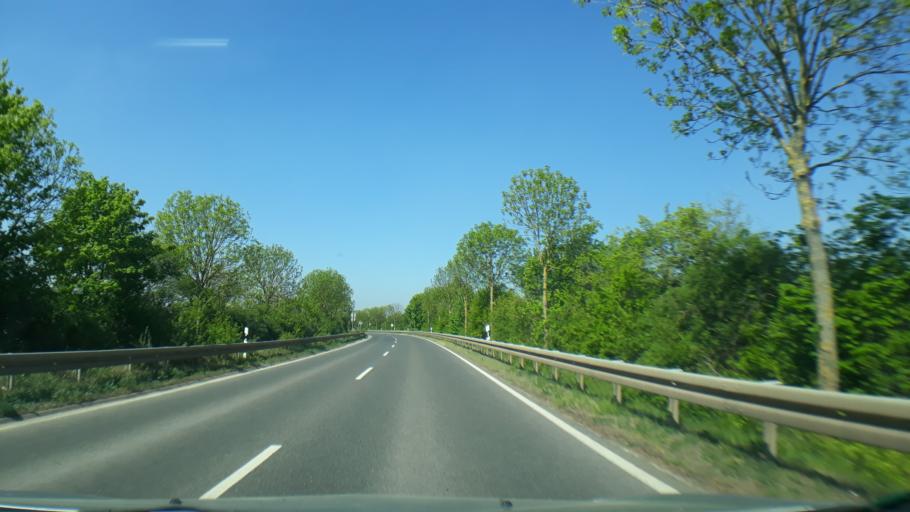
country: DE
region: North Rhine-Westphalia
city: Zulpich
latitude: 50.6964
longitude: 6.6865
